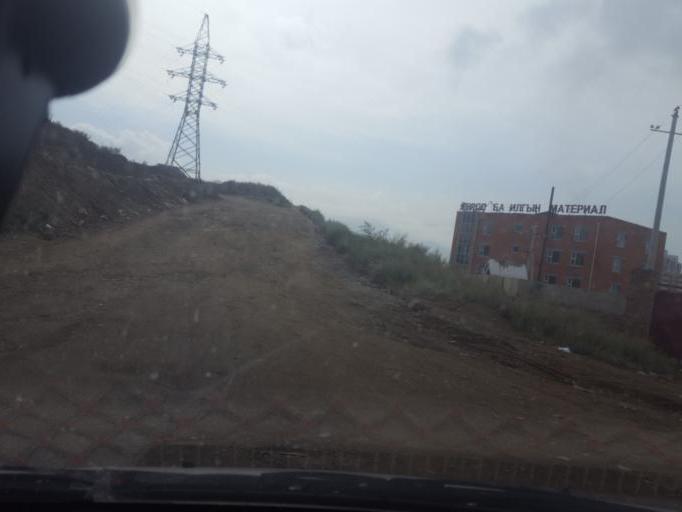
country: MN
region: Ulaanbaatar
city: Ulaanbaatar
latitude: 47.9155
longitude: 106.8006
